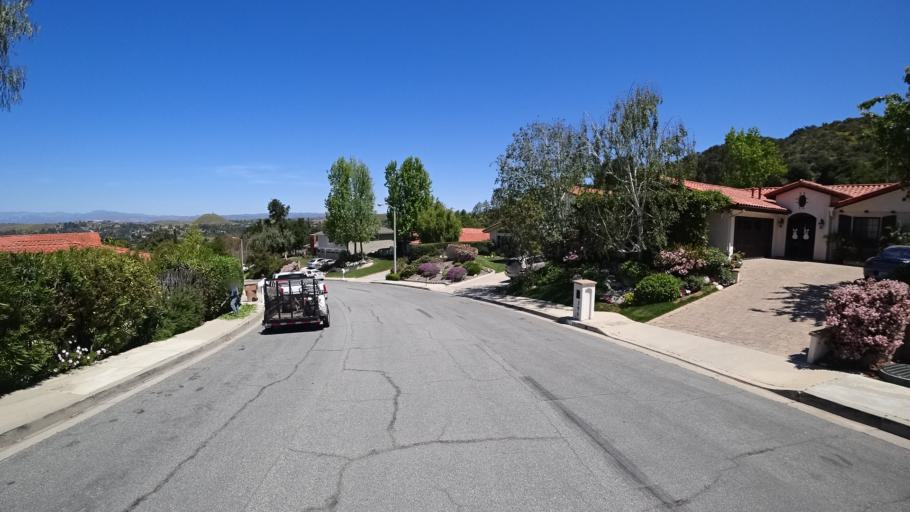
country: US
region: California
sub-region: Ventura County
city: Casa Conejo
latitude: 34.1731
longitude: -118.8962
